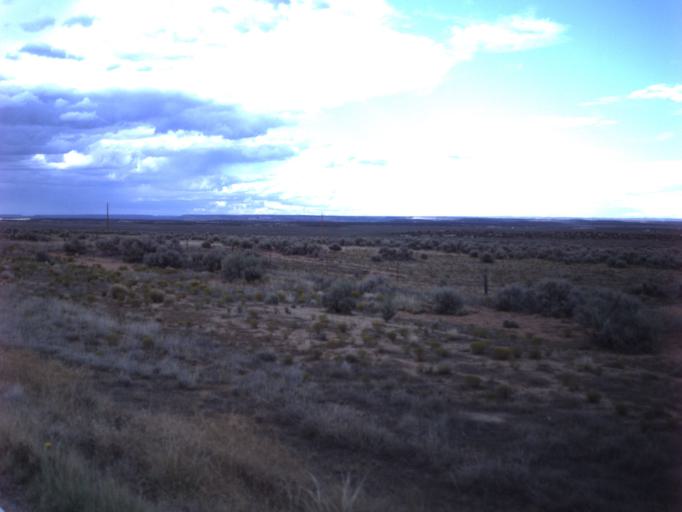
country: US
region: Utah
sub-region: San Juan County
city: Blanding
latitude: 37.3916
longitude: -109.3392
